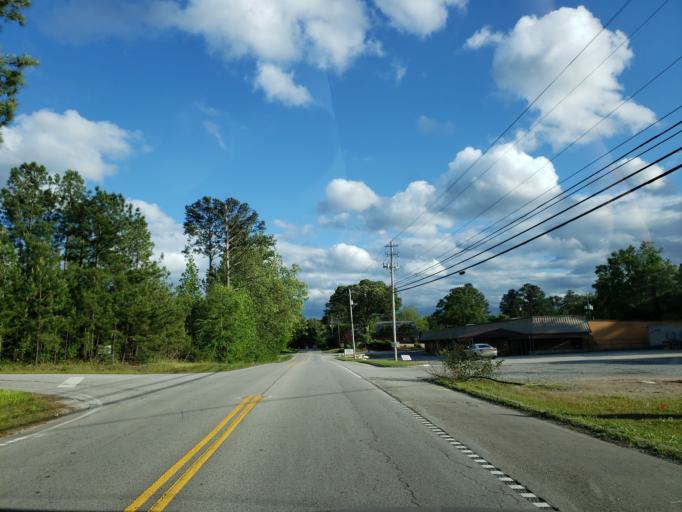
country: US
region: Georgia
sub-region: Haralson County
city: Tallapoosa
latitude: 33.7616
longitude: -85.2940
